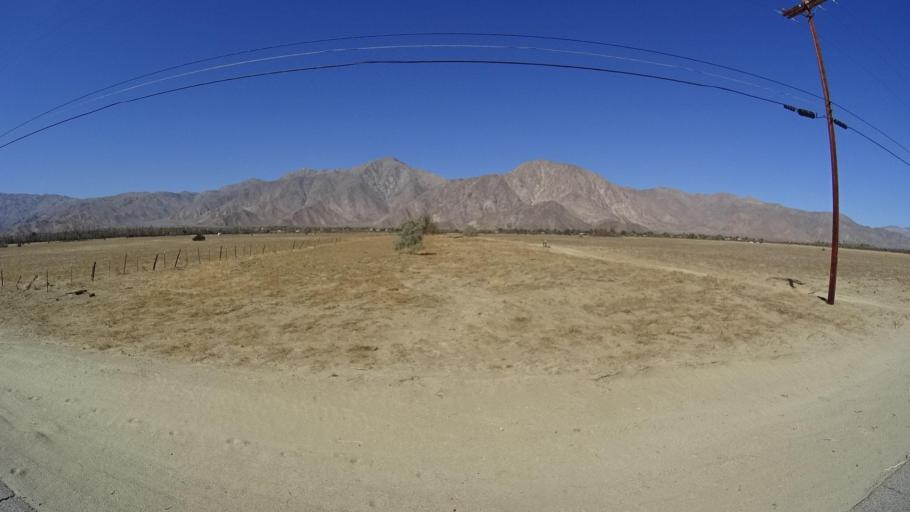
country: US
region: California
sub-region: San Diego County
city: Borrego Springs
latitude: 33.2809
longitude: -116.3664
